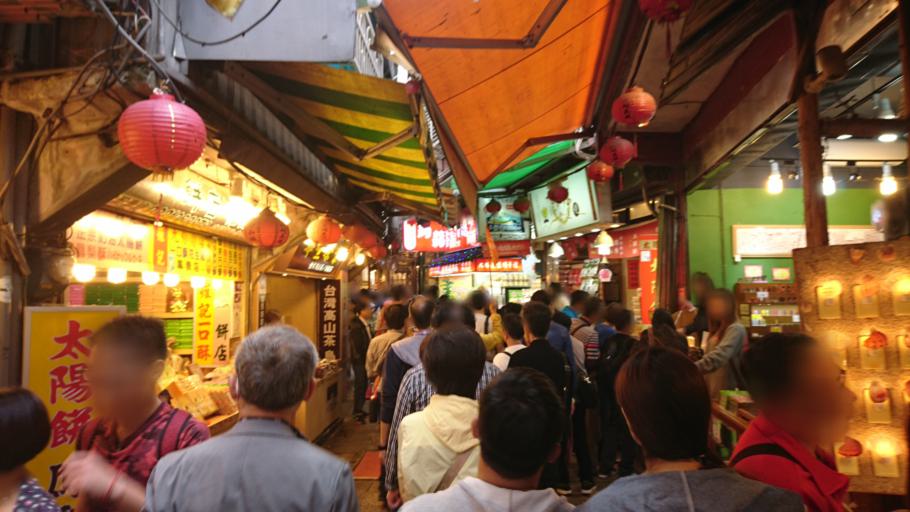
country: TW
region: Taiwan
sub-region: Keelung
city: Keelung
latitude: 25.1085
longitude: 121.8449
